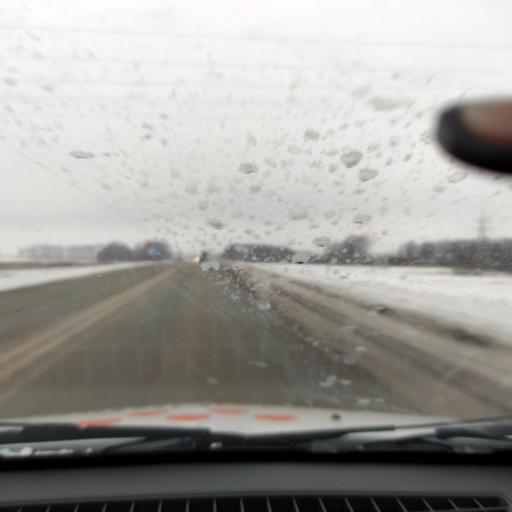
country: RU
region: Bashkortostan
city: Mikhaylovka
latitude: 54.8172
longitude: 55.8427
